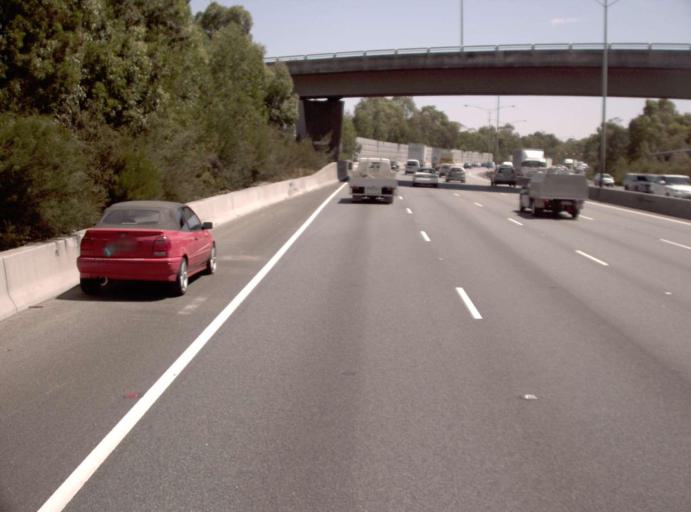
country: AU
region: Victoria
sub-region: Stonnington
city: Glen Iris
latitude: -37.8679
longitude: 145.0623
